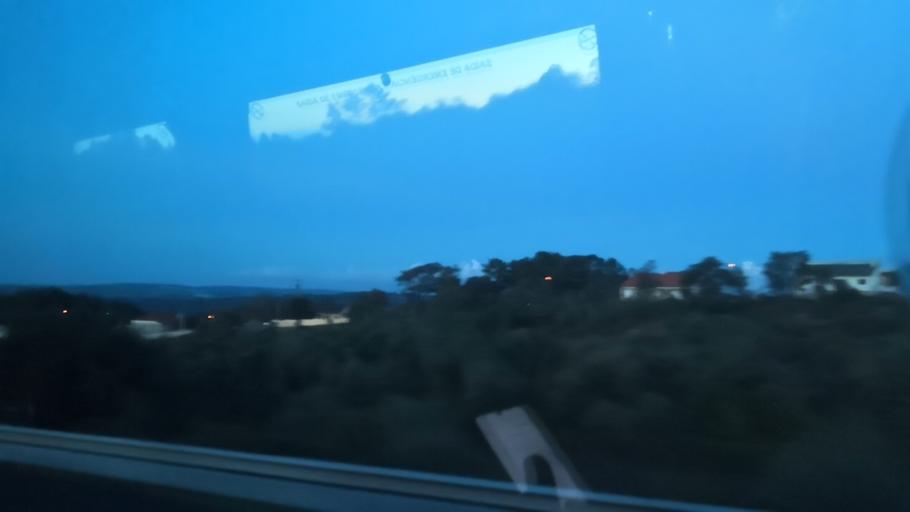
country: PT
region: Leiria
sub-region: Leiria
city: Santa Catarina da Serra
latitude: 39.6981
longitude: -8.6957
